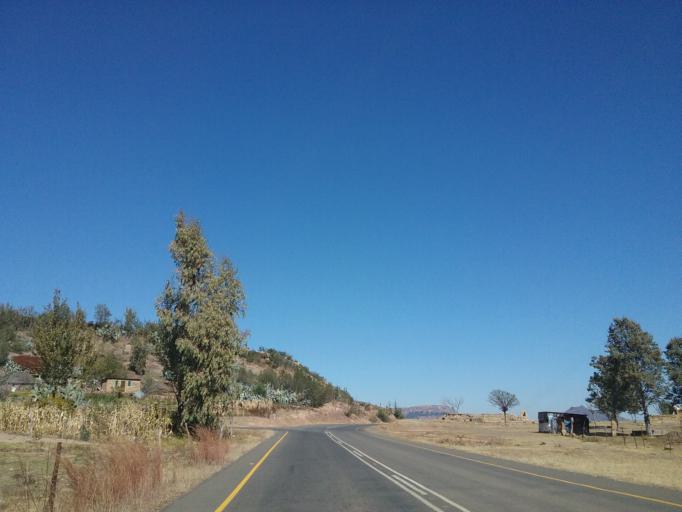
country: LS
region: Maseru
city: Nako
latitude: -29.4642
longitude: 27.6440
